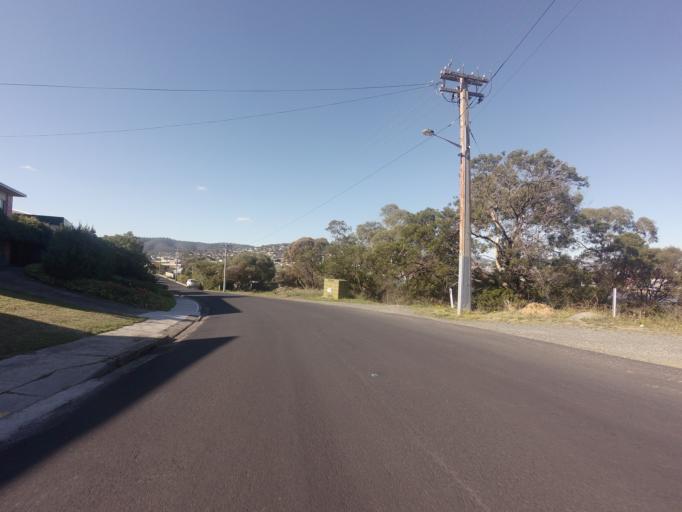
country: AU
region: Tasmania
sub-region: Clarence
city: Bellerive
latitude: -42.8724
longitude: 147.3603
